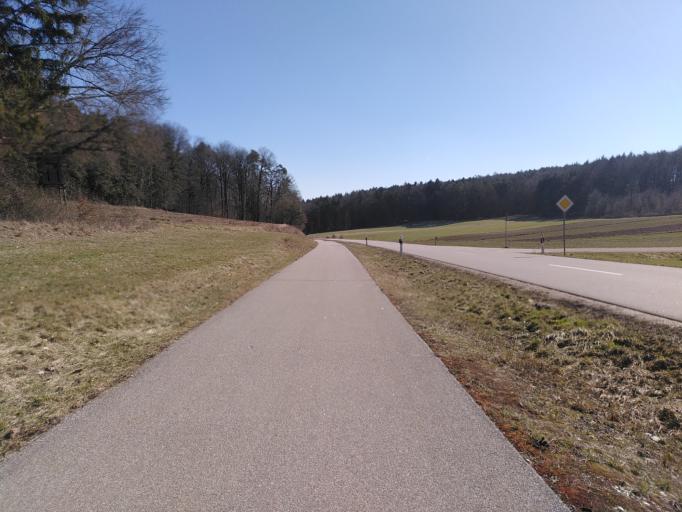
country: DE
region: Bavaria
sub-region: Upper Palatinate
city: Sinzing
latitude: 49.0026
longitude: 12.0121
